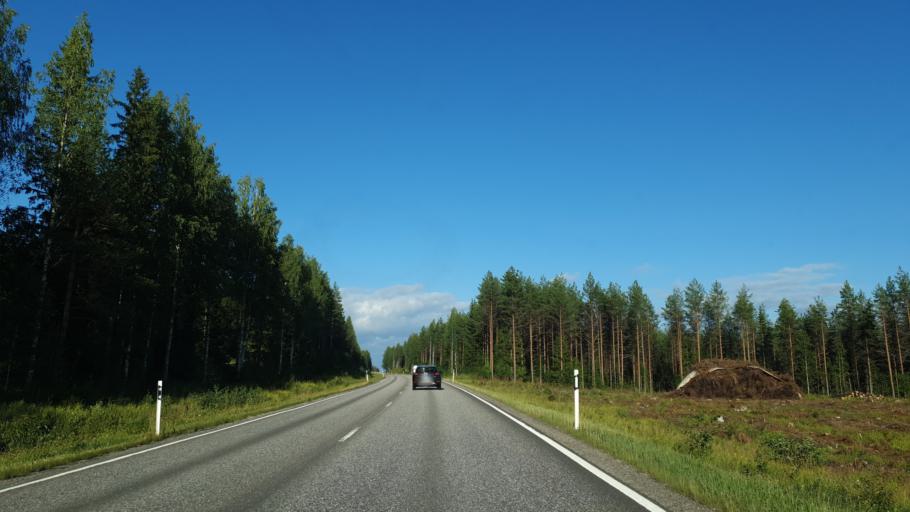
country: FI
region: North Karelia
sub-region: Joensuu
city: Outokumpu
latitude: 62.5198
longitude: 29.0208
